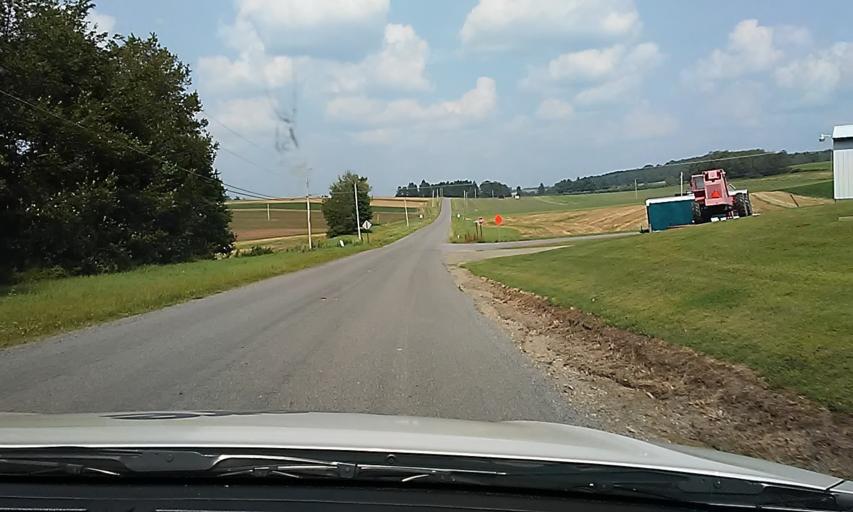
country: US
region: Pennsylvania
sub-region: Potter County
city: Coudersport
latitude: 41.7963
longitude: -77.8877
